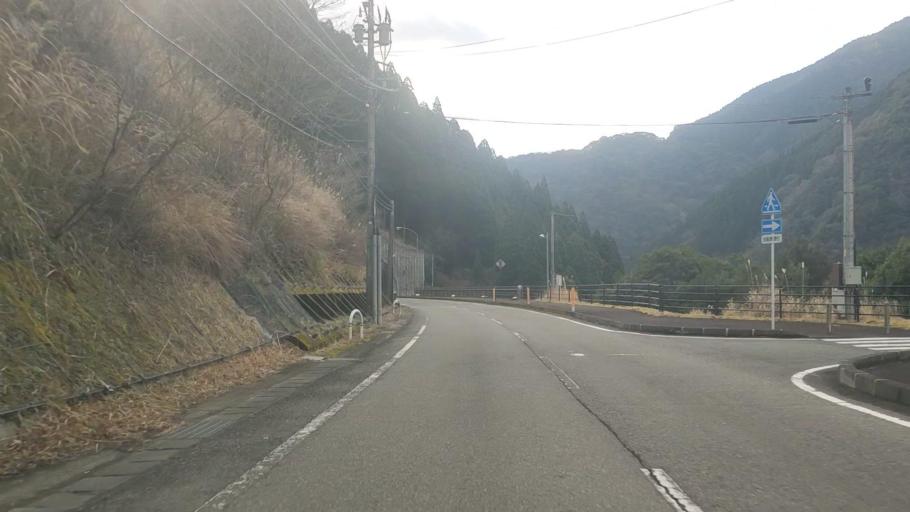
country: JP
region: Kumamoto
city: Hitoyoshi
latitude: 32.3944
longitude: 130.8270
